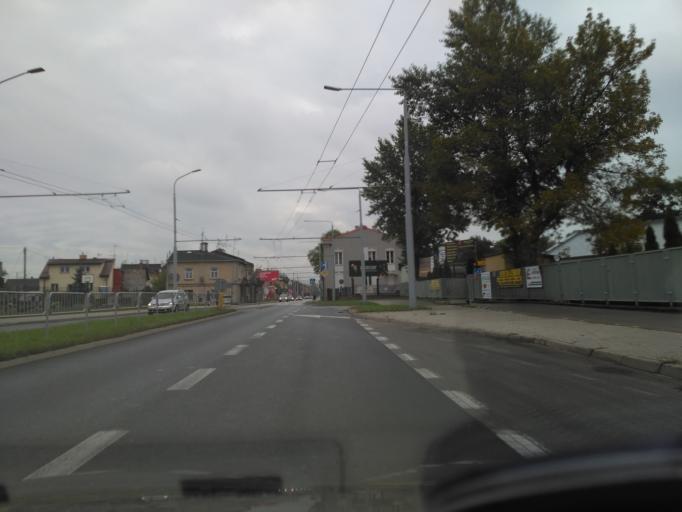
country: PL
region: Lublin Voivodeship
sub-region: Powiat lubelski
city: Lublin
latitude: 51.2370
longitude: 22.5778
